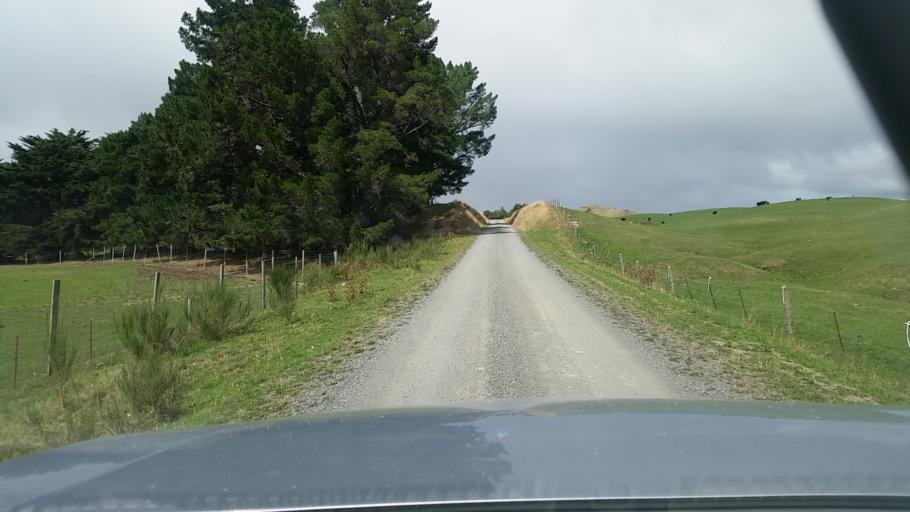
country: NZ
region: Marlborough
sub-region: Marlborough District
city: Blenheim
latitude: -41.7469
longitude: 173.8948
